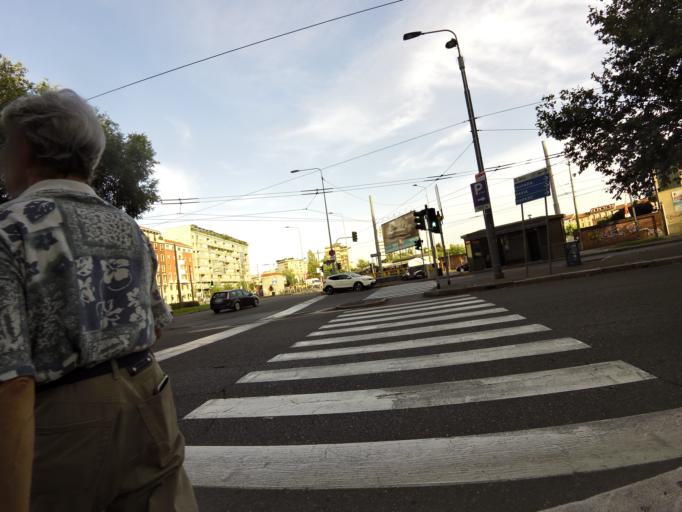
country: IT
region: Lombardy
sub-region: Citta metropolitana di Milano
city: Milano
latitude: 45.4472
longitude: 9.2095
